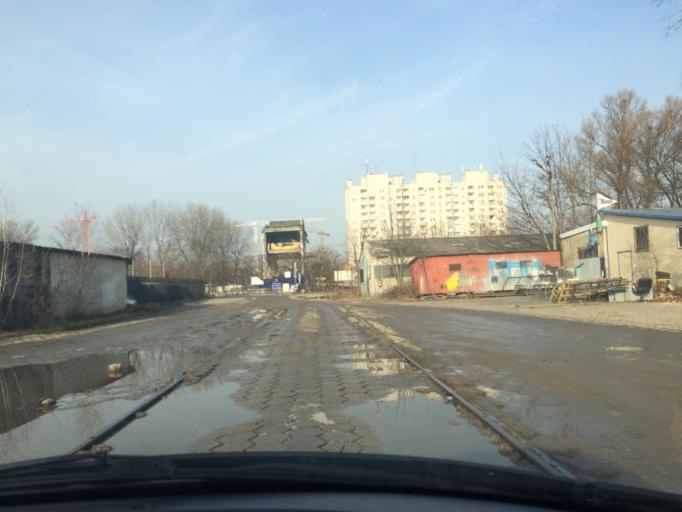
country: PL
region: Lesser Poland Voivodeship
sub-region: Krakow
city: Krakow
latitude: 50.0630
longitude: 20.0110
